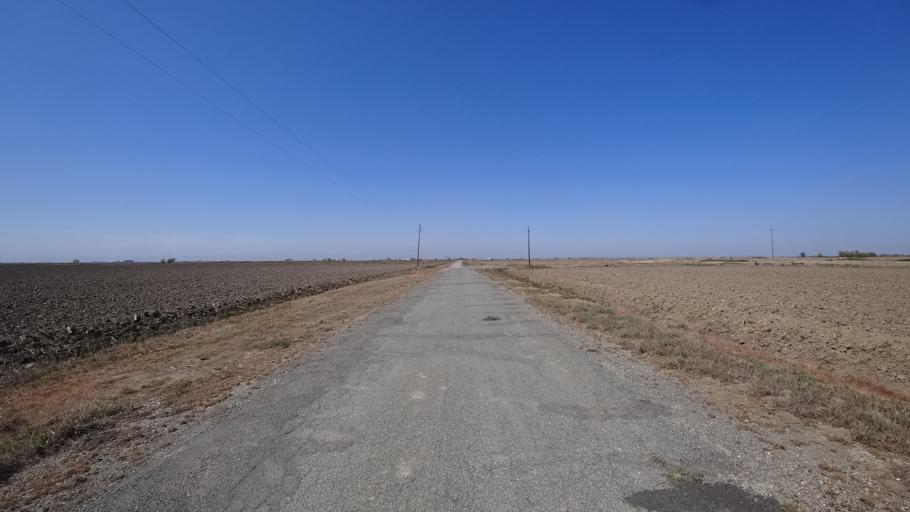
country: US
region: California
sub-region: Glenn County
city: Willows
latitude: 39.4929
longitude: -122.0922
